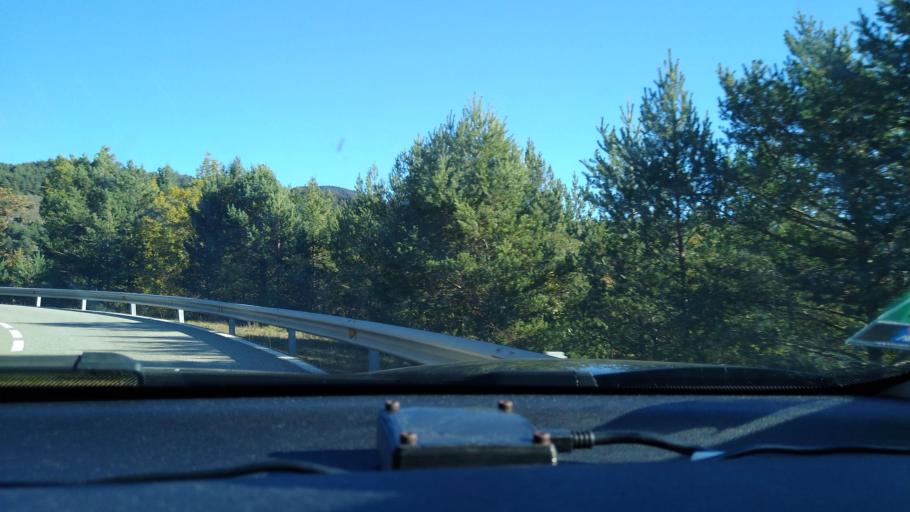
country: ES
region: Catalonia
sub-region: Provincia de Barcelona
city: Vallcebre
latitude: 42.2203
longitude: 1.8247
